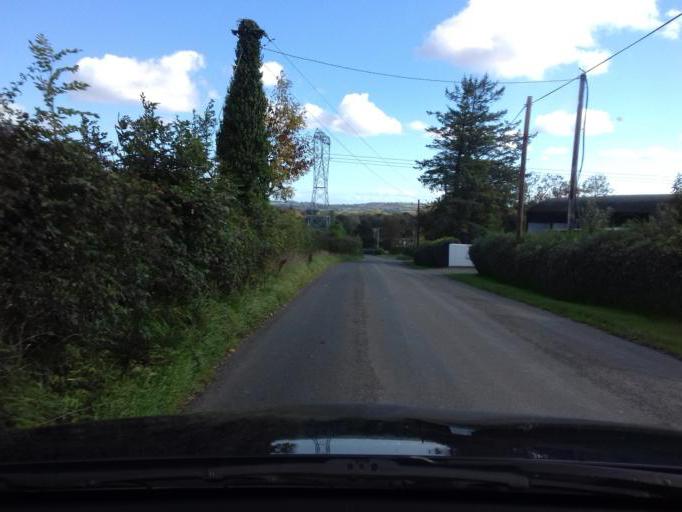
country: IE
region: Leinster
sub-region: An Mhi
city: Slane
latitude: 53.6872
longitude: -6.5197
